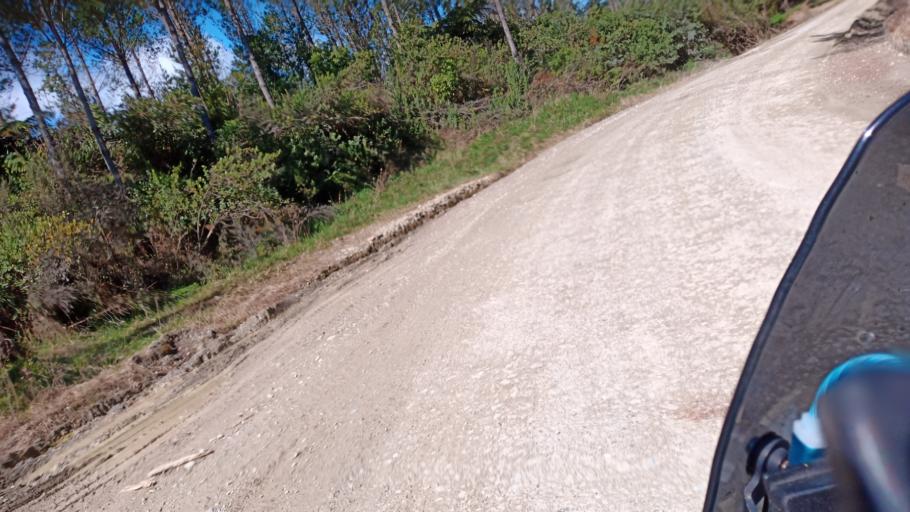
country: NZ
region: Gisborne
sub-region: Gisborne District
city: Gisborne
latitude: -38.9067
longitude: 177.8066
